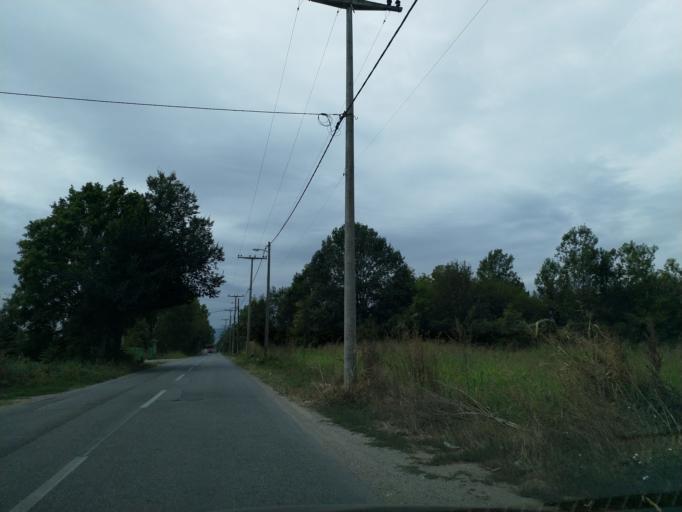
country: RS
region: Central Serbia
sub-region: Pomoravski Okrug
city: Paracin
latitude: 43.8508
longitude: 21.3888
